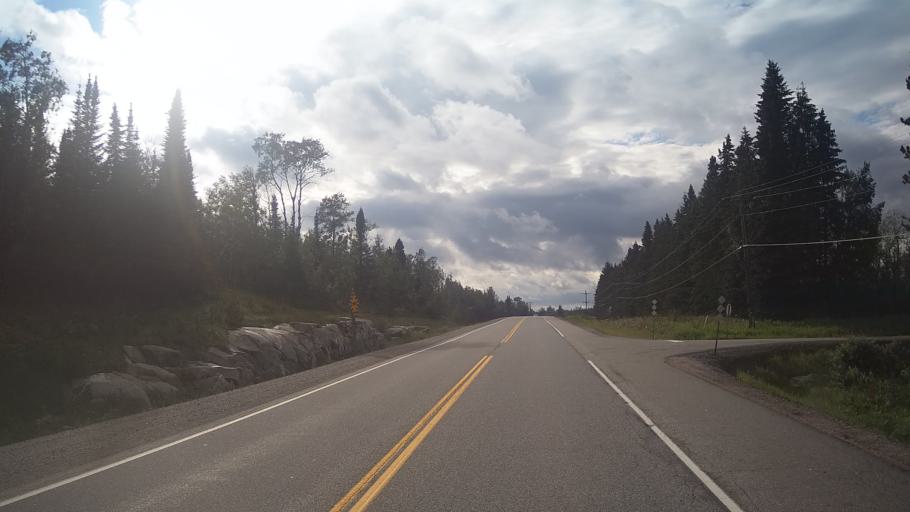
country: CA
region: Ontario
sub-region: Rainy River District
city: Atikokan
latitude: 49.0230
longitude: -90.4467
